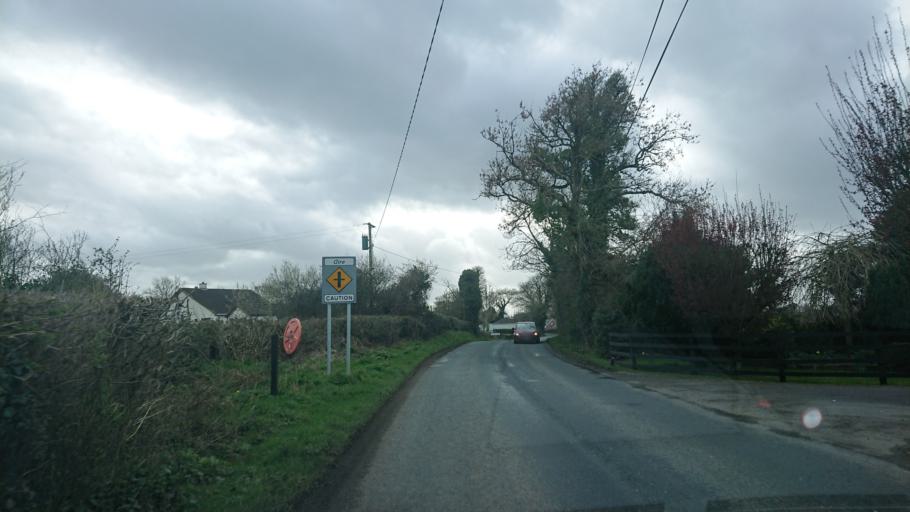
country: IE
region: Leinster
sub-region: Kildare
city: Naas
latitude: 53.1773
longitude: -6.6724
